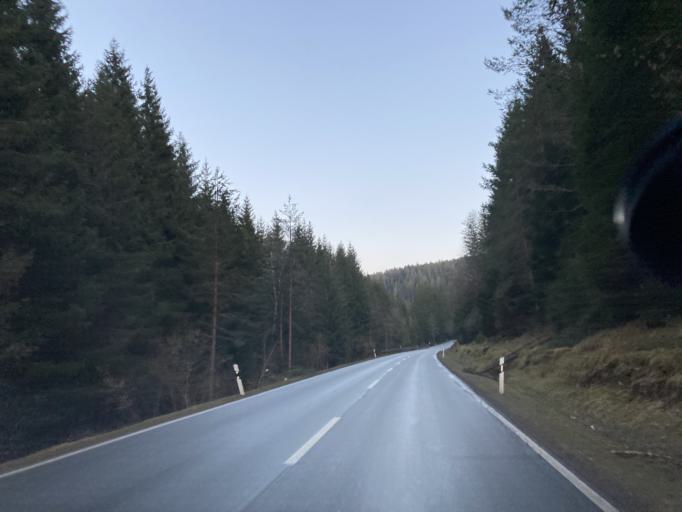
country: DE
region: Baden-Wuerttemberg
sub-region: Karlsruhe Region
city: Neuweiler
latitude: 48.6874
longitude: 8.5710
